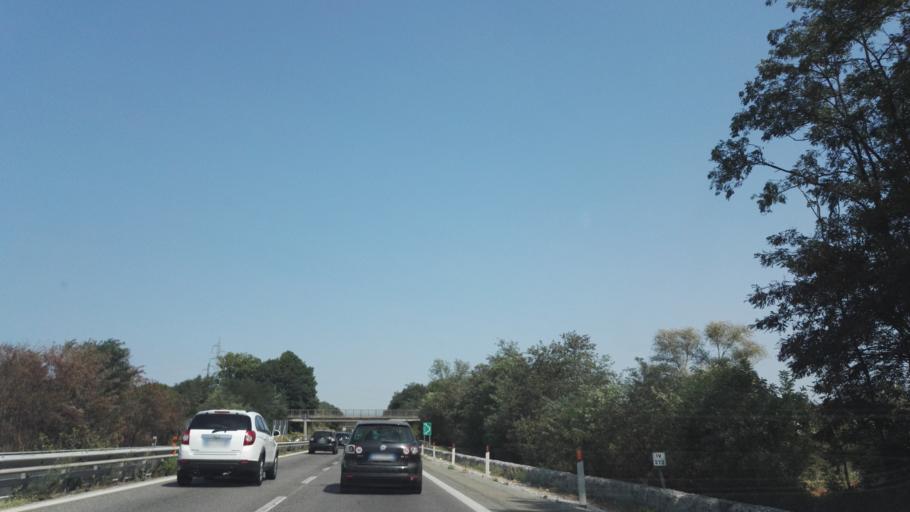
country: IT
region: Calabria
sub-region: Provincia di Cosenza
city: Santo Stefano di Rogliano
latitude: 39.2069
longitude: 16.3093
